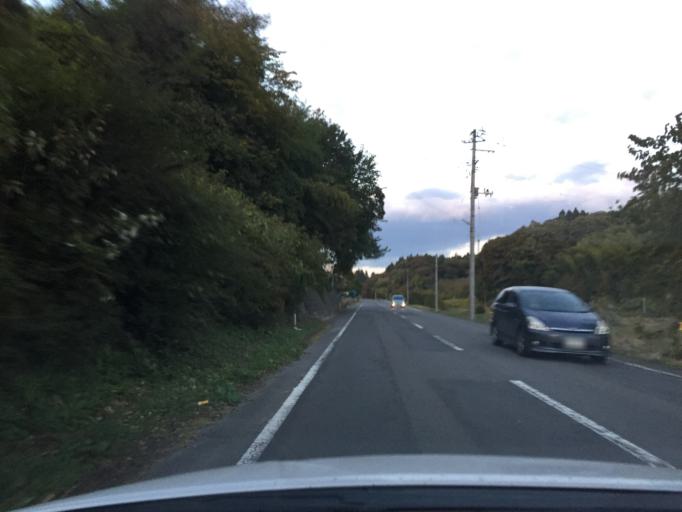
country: JP
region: Fukushima
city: Miharu
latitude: 37.4715
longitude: 140.4415
